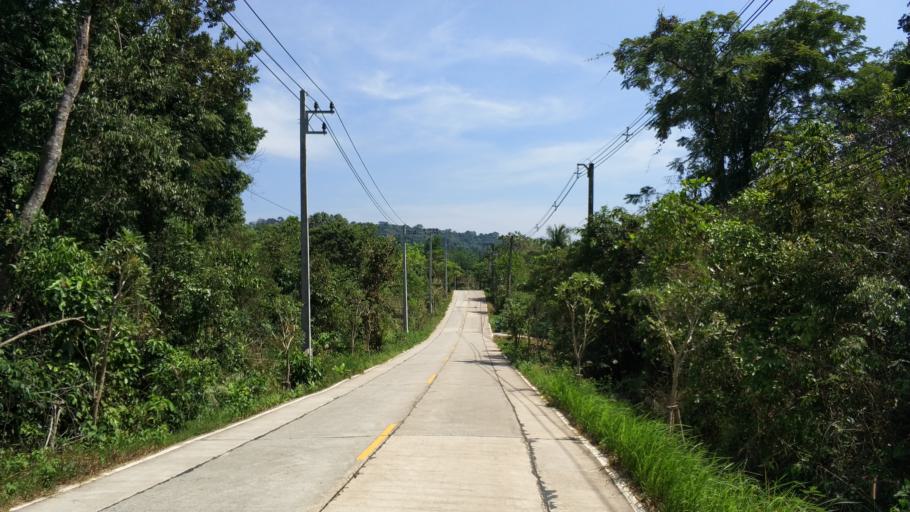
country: TH
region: Trat
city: Ko Kut
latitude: 11.6275
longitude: 102.5466
